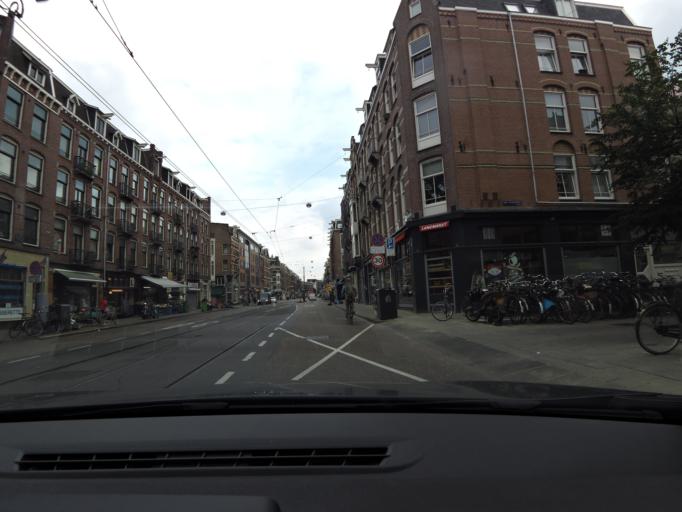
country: NL
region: North Holland
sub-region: Gemeente Amsterdam
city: Amsterdam
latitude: 52.3538
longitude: 4.9021
